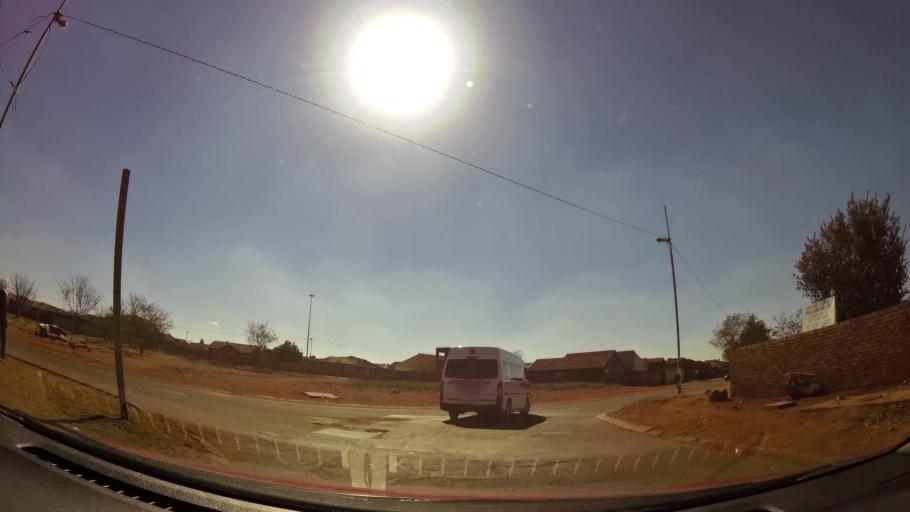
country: ZA
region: Gauteng
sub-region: City of Johannesburg Metropolitan Municipality
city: Soweto
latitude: -26.2424
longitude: 27.8068
